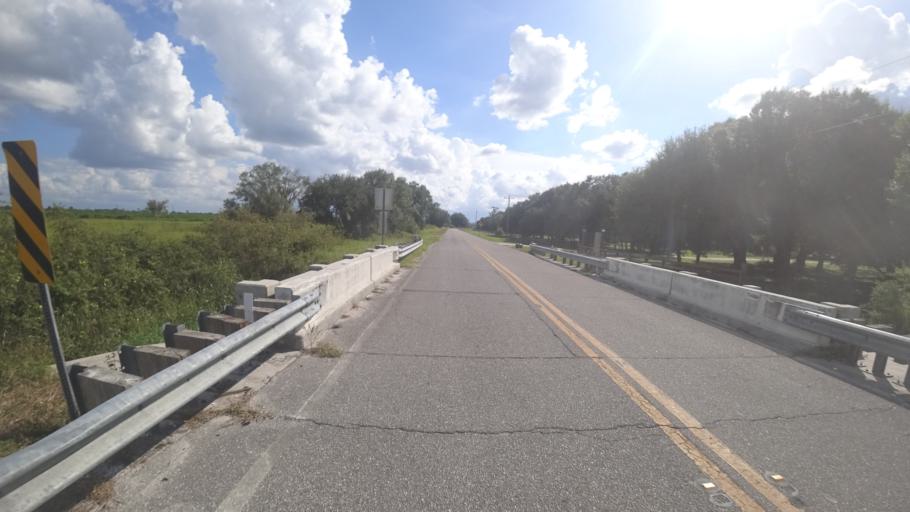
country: US
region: Florida
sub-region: DeSoto County
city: Nocatee
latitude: 27.2834
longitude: -82.1135
